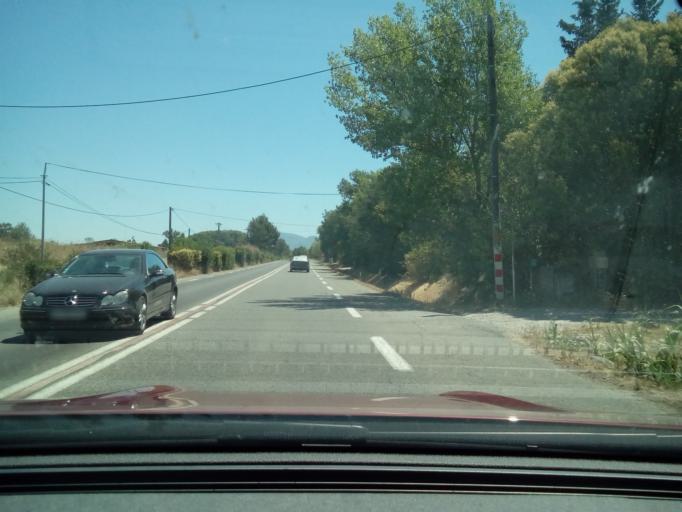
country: FR
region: Provence-Alpes-Cote d'Azur
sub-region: Departement des Bouches-du-Rhone
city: Chateauneuf-le-Rouge
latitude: 43.4724
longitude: 5.5806
